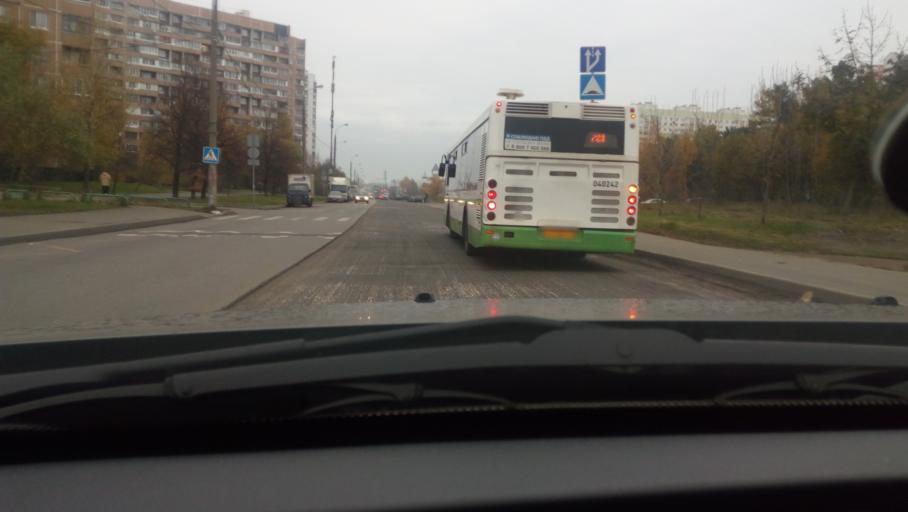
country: RU
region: Moskovskaya
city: Reutov
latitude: 55.7397
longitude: 37.8754
